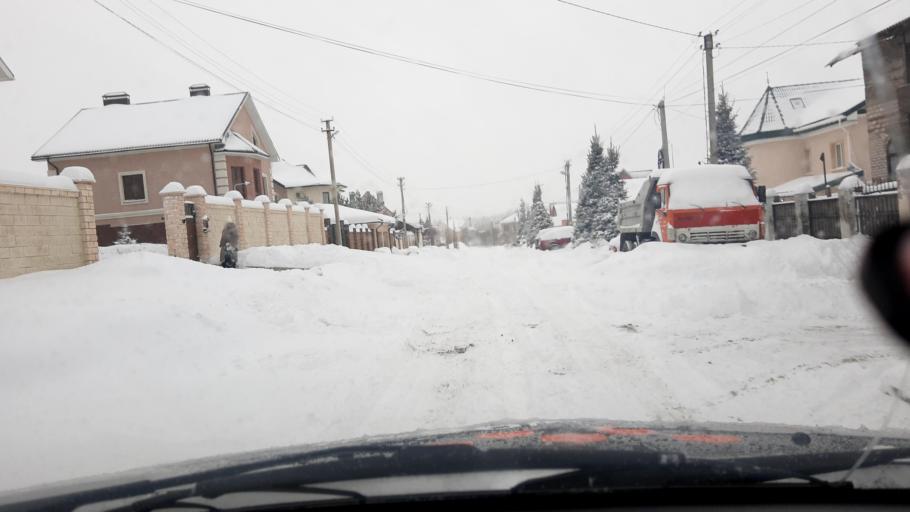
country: RU
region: Bashkortostan
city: Ufa
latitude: 54.6060
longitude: 55.9558
